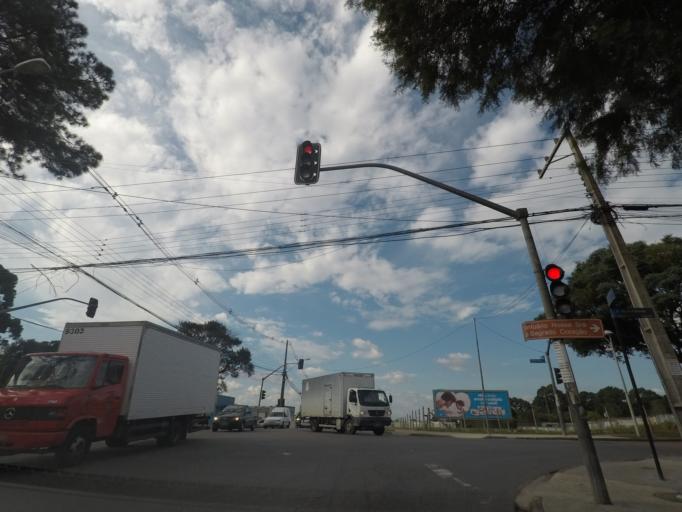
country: BR
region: Parana
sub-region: Sao Jose Dos Pinhais
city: Sao Jose dos Pinhais
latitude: -25.5324
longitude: -49.2975
